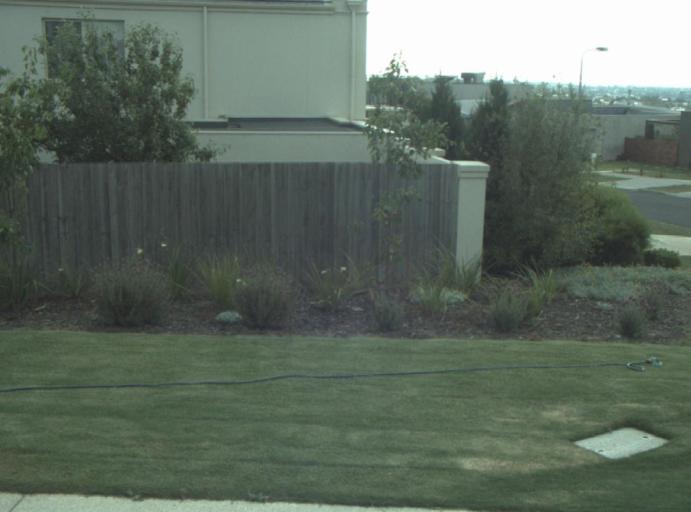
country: AU
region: Victoria
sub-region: Greater Geelong
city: Wandana Heights
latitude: -38.1556
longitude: 144.3162
